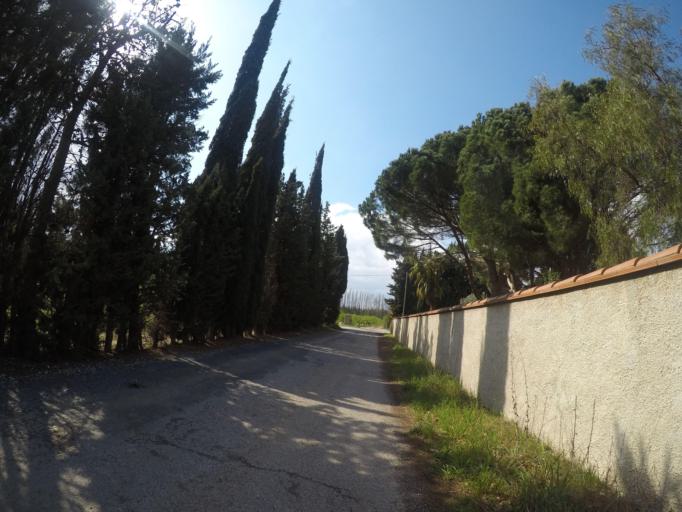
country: FR
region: Languedoc-Roussillon
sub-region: Departement des Pyrenees-Orientales
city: Pezilla-la-Riviere
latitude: 42.6699
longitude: 2.7684
